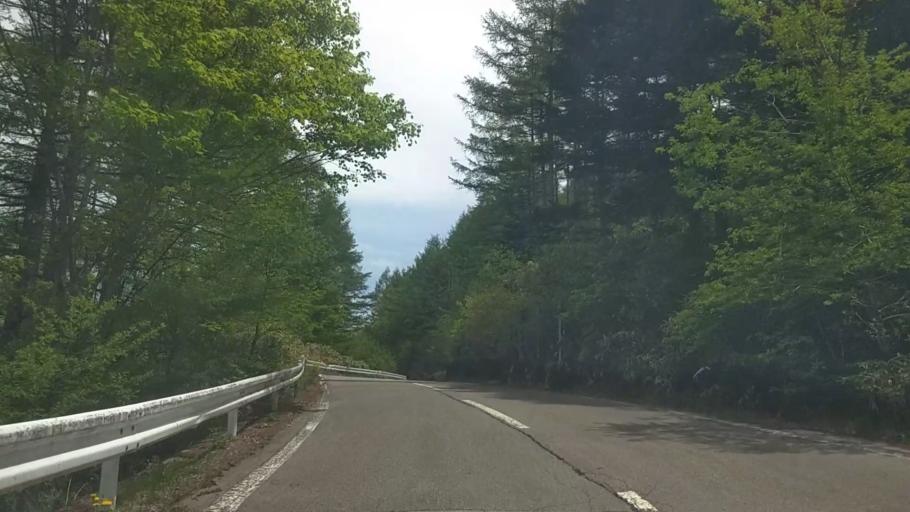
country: JP
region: Nagano
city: Saku
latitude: 36.0970
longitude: 138.3862
